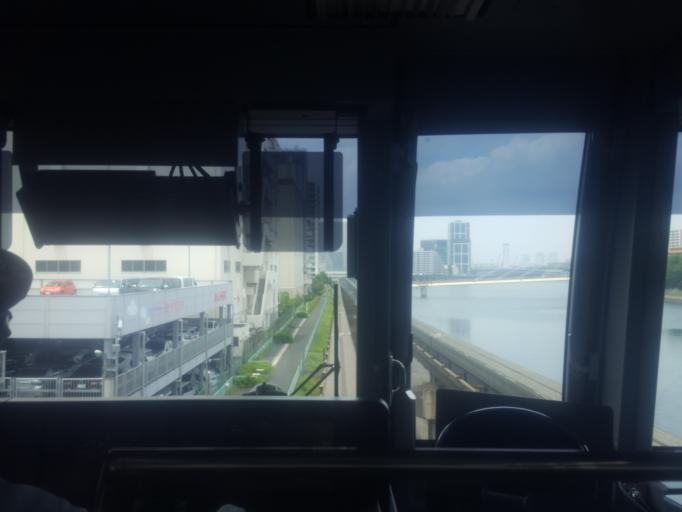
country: JP
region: Kanagawa
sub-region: Kawasaki-shi
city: Kawasaki
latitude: 35.5970
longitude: 139.7472
